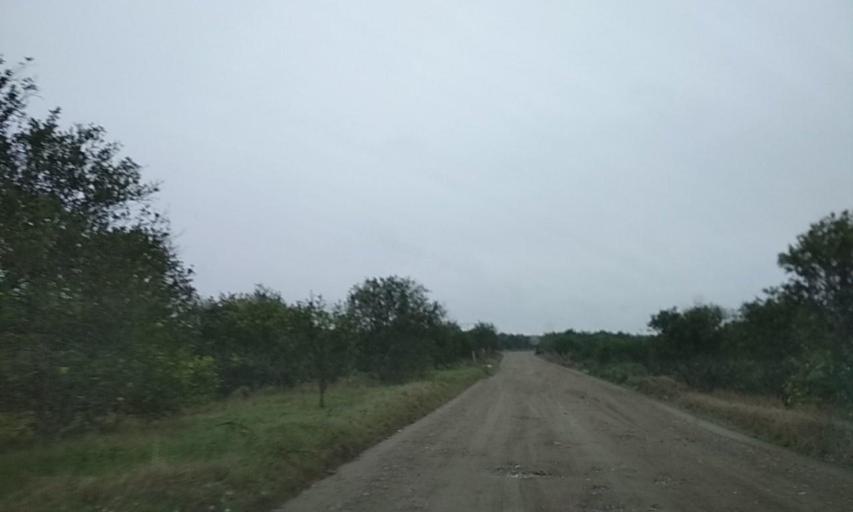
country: MX
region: Veracruz
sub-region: Papantla
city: El Chote
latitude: 20.3385
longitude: -97.3903
